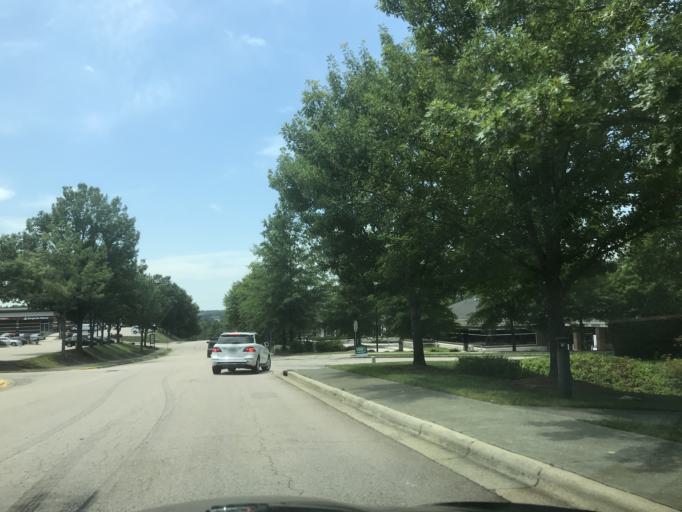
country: US
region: North Carolina
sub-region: Wake County
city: Wake Forest
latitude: 35.9447
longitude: -78.5420
